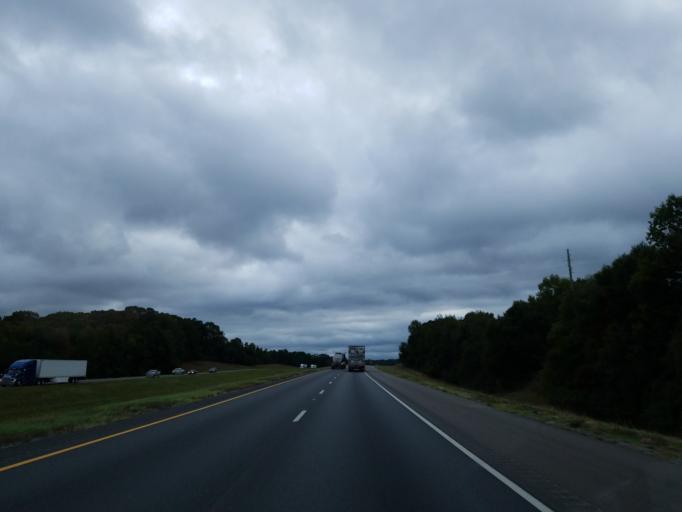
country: US
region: Alabama
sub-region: Hale County
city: Moundville
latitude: 33.0642
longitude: -87.6986
